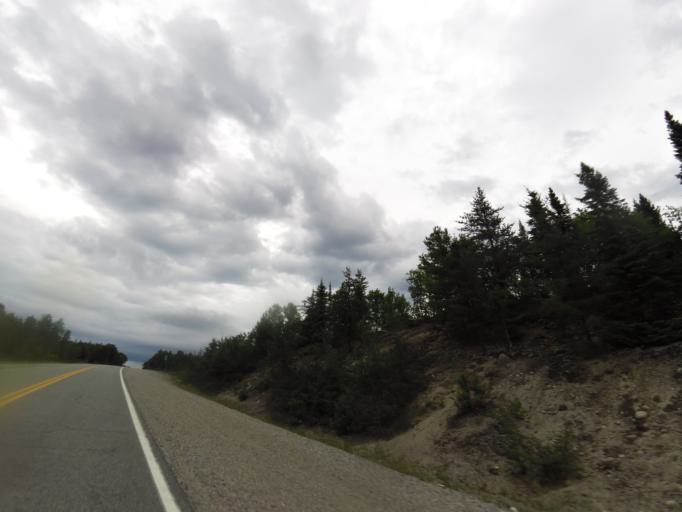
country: CA
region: Quebec
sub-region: Abitibi-Temiscamingue
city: Amos
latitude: 48.9549
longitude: -77.9571
